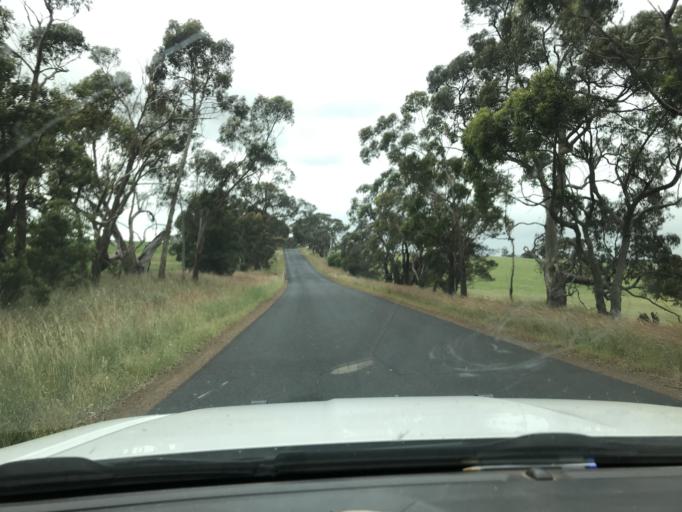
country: AU
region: Victoria
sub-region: Southern Grampians
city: Hamilton
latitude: -37.1821
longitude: 141.5629
